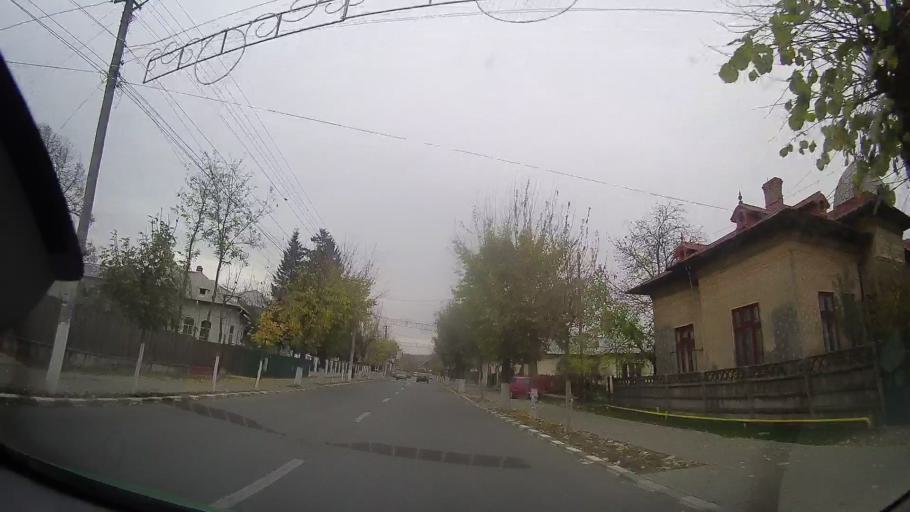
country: RO
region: Prahova
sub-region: Oras Urlati
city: Urlati
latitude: 44.9875
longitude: 26.2341
